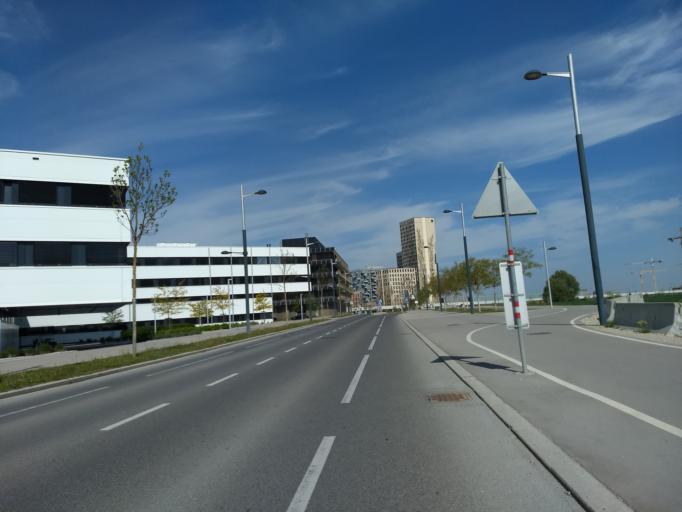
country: AT
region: Lower Austria
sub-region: Politischer Bezirk Ganserndorf
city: Gross-Enzersdorf
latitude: 48.2223
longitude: 16.5114
